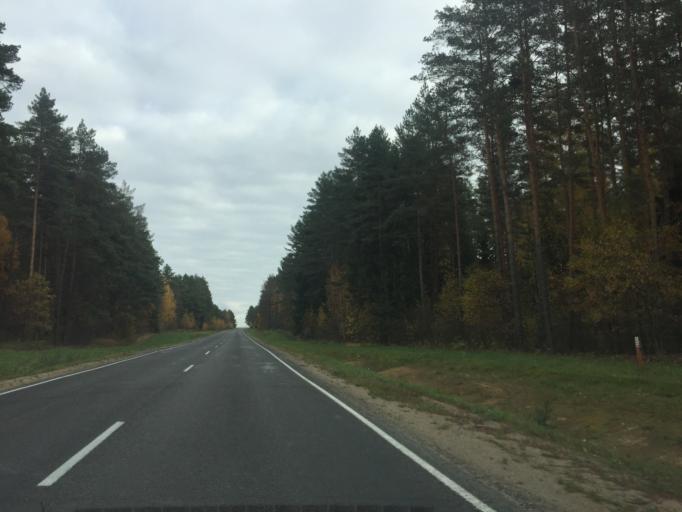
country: BY
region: Grodnenskaya
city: Astravyets
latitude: 54.7893
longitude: 26.0801
